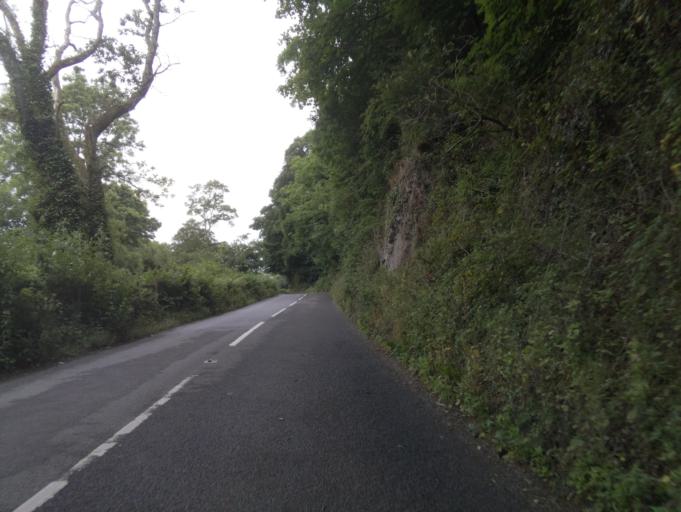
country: GB
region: England
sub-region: Devon
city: Chudleigh
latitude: 50.6345
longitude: -3.6395
